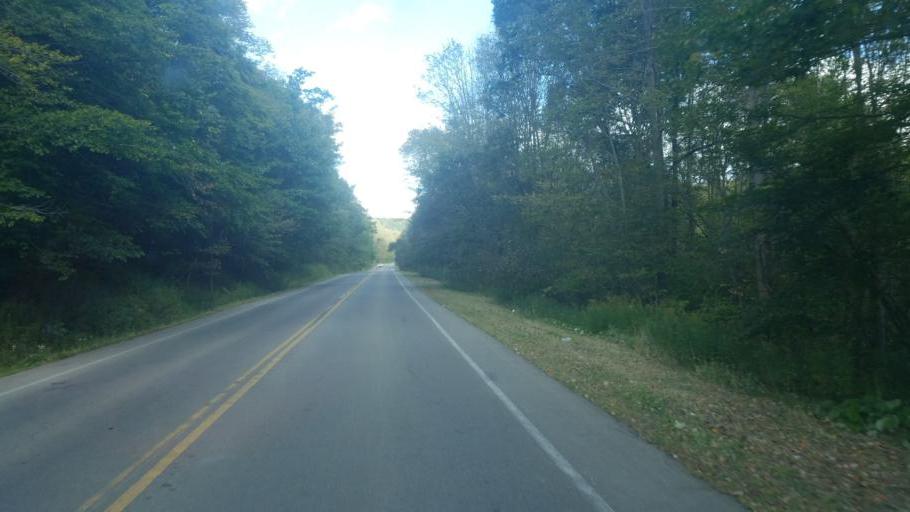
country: US
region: New York
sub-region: Allegany County
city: Cuba
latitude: 42.2263
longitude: -78.3116
